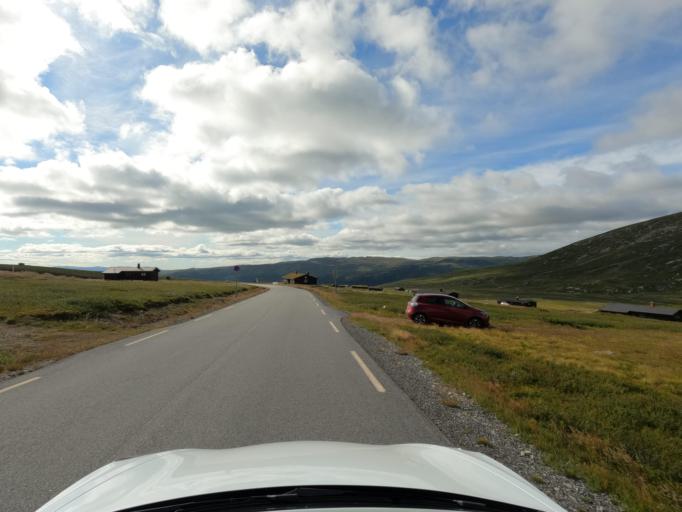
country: NO
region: Telemark
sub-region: Tinn
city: Rjukan
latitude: 60.1632
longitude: 8.6042
